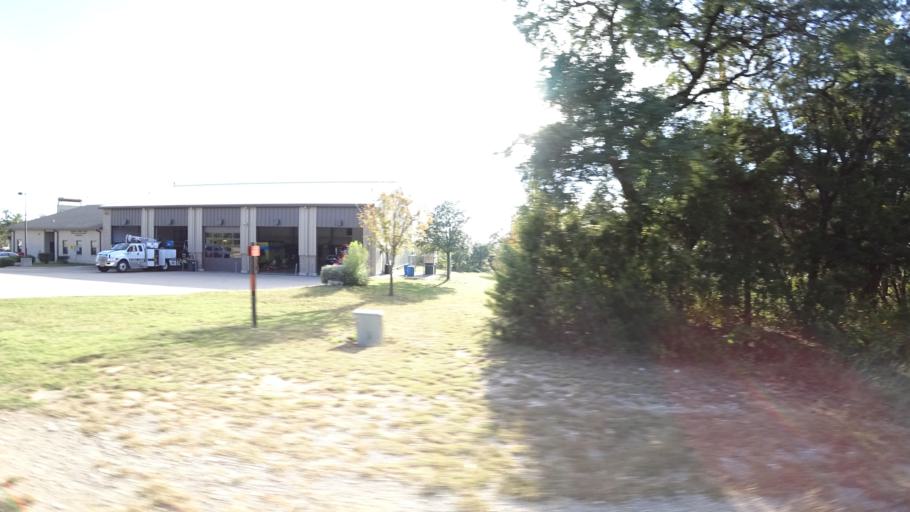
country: US
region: Texas
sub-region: Travis County
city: Barton Creek
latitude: 30.2401
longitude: -97.9199
